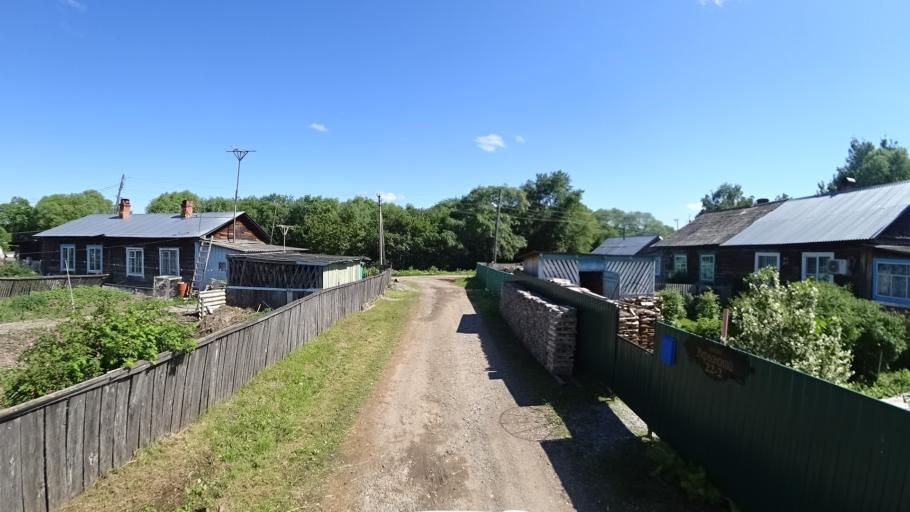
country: RU
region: Khabarovsk Krai
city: Khor
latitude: 47.8856
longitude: 135.0287
